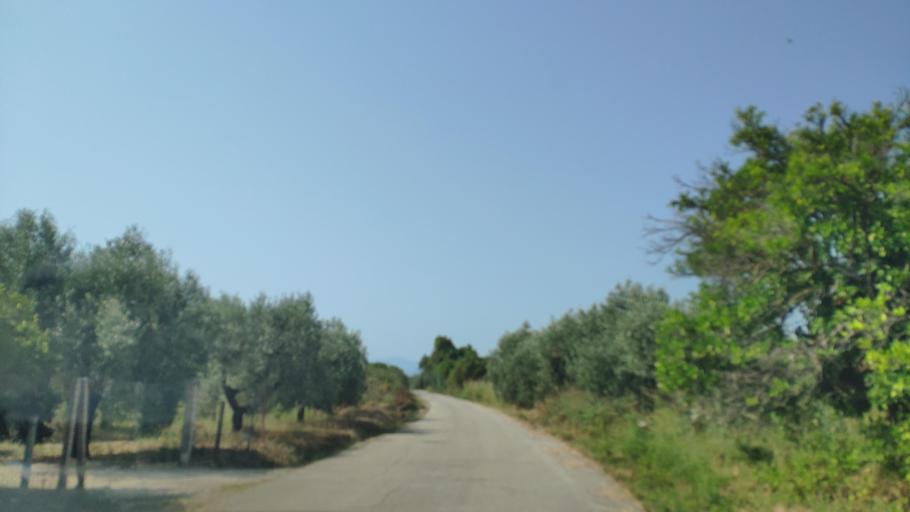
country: GR
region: Epirus
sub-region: Nomos Artas
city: Kompoti
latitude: 39.0650
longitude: 21.0763
